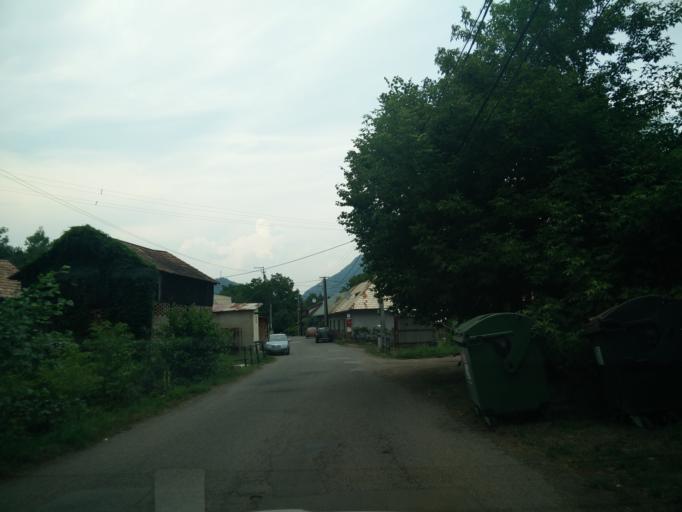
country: SK
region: Banskobystricky
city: Ziar nad Hronom
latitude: 48.5793
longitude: 18.8971
